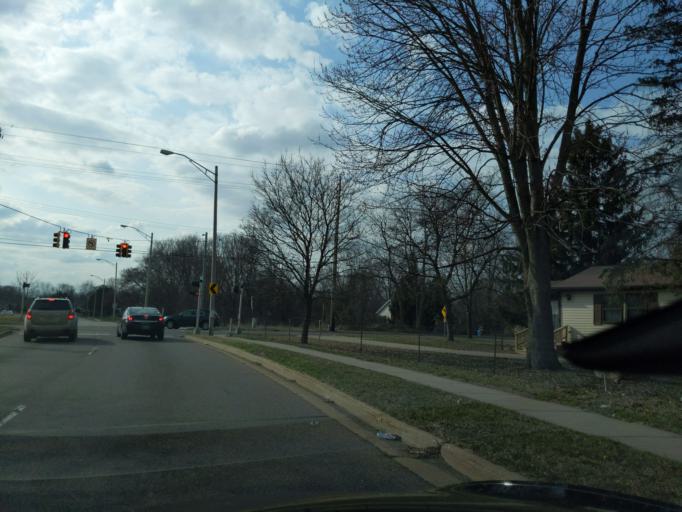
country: US
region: Michigan
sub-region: Ingham County
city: Holt
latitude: 42.6625
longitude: -84.5628
